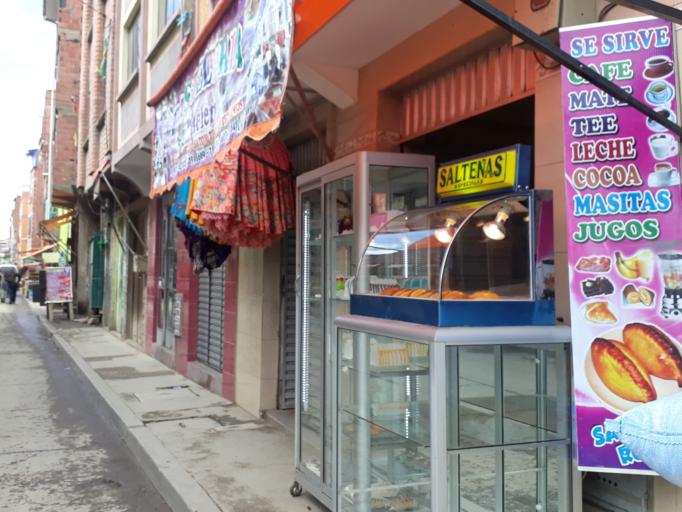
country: BO
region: La Paz
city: Achacachi
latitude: -16.0415
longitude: -68.6854
